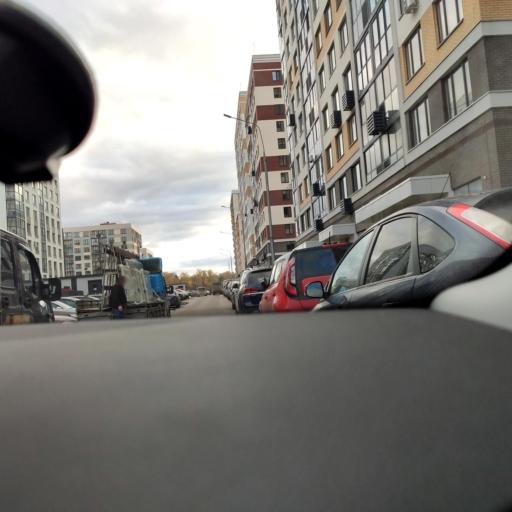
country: RU
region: Moskovskaya
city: Mosrentgen
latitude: 55.5945
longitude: 37.4607
